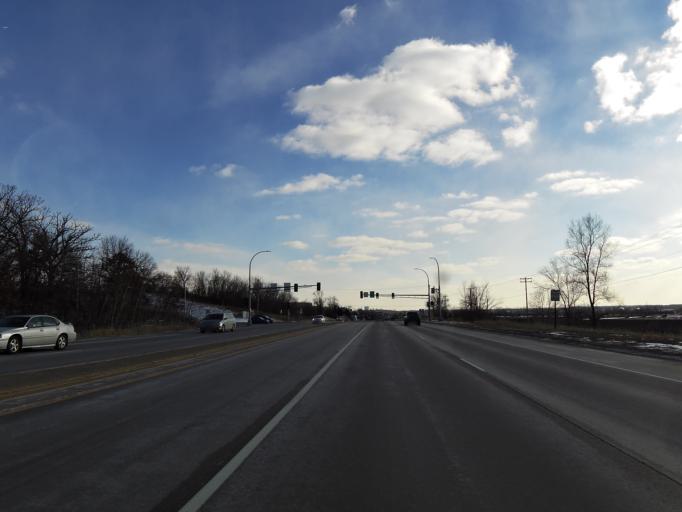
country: US
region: Minnesota
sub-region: Dakota County
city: Mendota Heights
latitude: 44.8618
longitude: -93.1294
